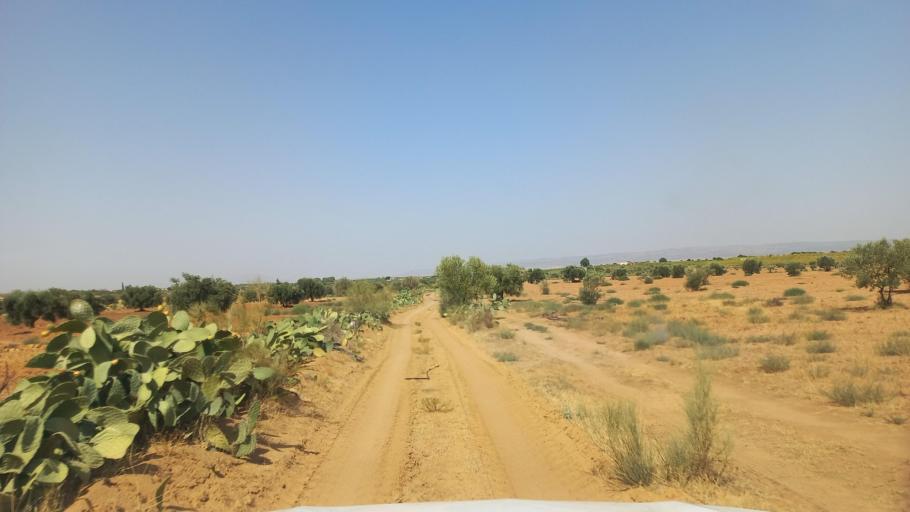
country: TN
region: Al Qasrayn
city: Kasserine
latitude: 35.2404
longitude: 9.0632
